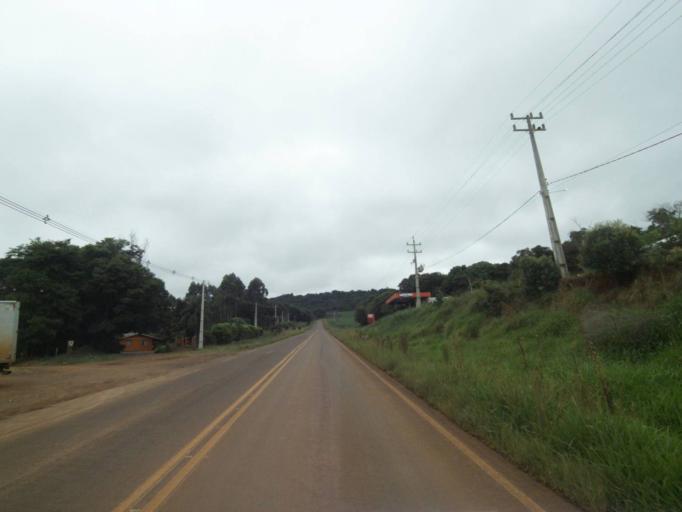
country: BR
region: Parana
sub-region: Pitanga
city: Pitanga
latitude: -24.9254
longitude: -51.8729
